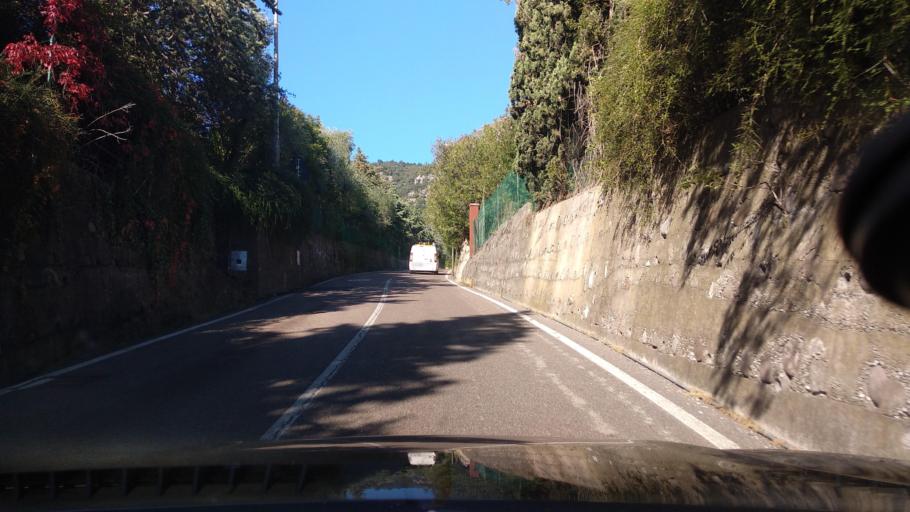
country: IT
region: Veneto
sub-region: Provincia di Verona
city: Garda
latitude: 45.5800
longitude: 10.7047
